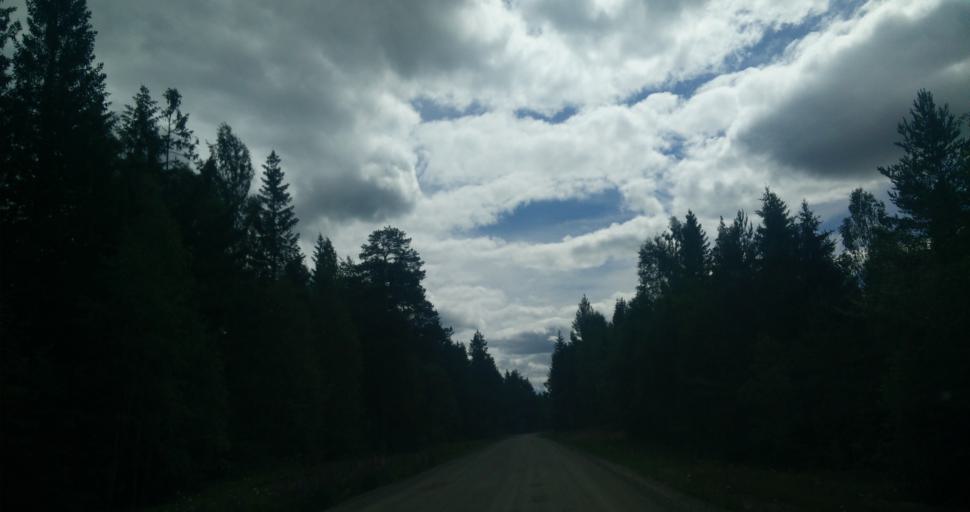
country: SE
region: Gaevleborg
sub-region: Nordanstigs Kommun
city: Bergsjoe
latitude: 62.1142
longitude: 17.0980
